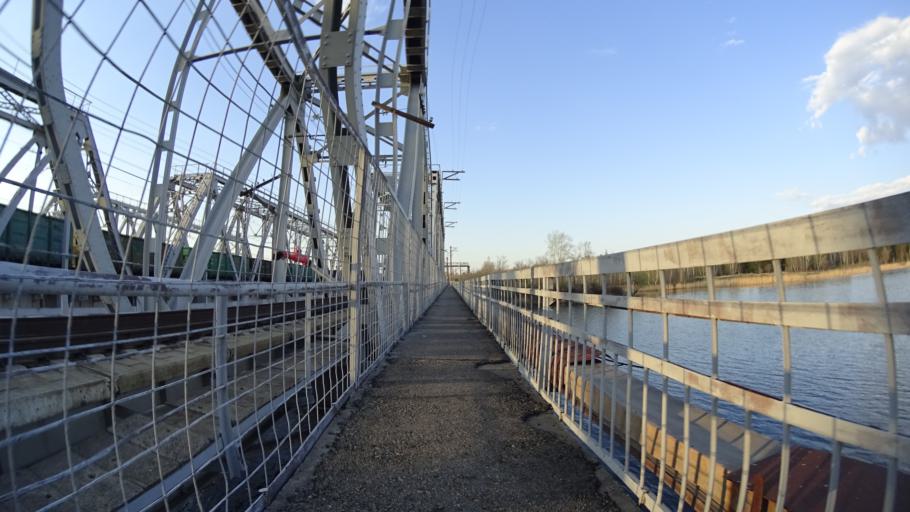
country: RU
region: Chelyabinsk
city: Troitsk
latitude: 54.0551
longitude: 61.6113
